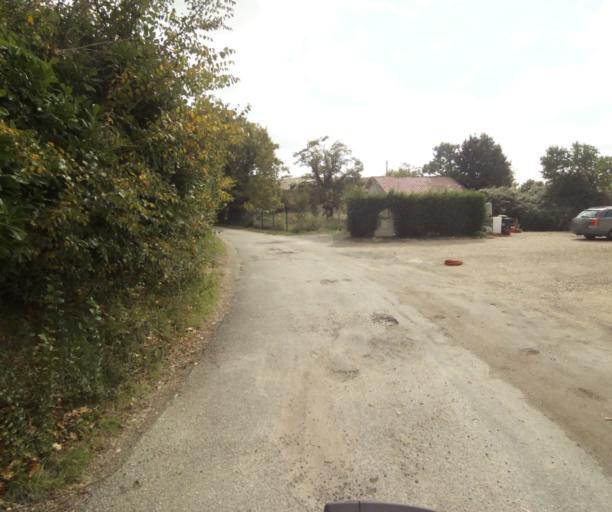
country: FR
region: Midi-Pyrenees
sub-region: Departement du Tarn-et-Garonne
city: Finhan
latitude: 43.9166
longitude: 1.2170
